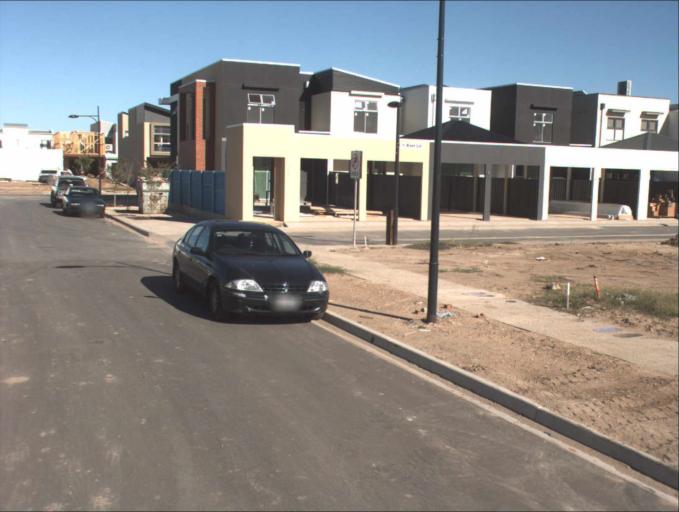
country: AU
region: South Australia
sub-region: Port Adelaide Enfield
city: Klemzig
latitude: -34.8634
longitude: 138.6265
